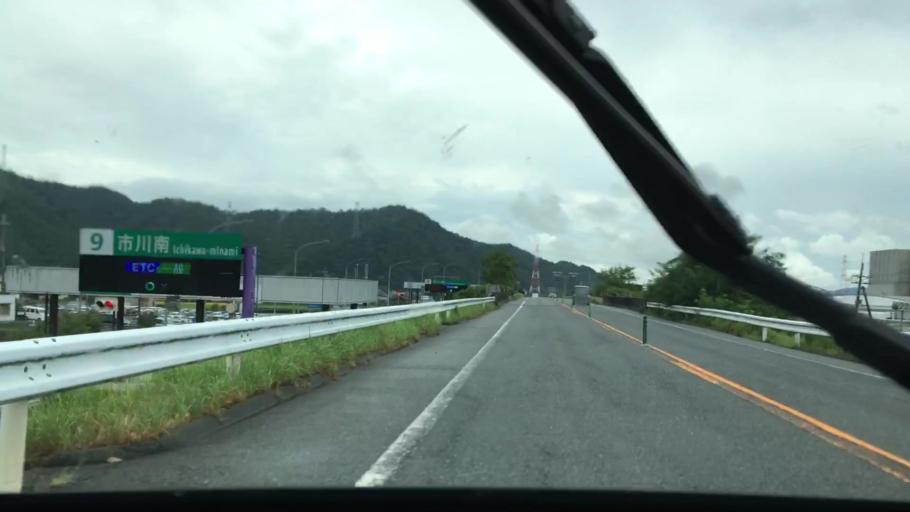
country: JP
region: Hyogo
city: Himeji
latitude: 34.9849
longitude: 134.7701
